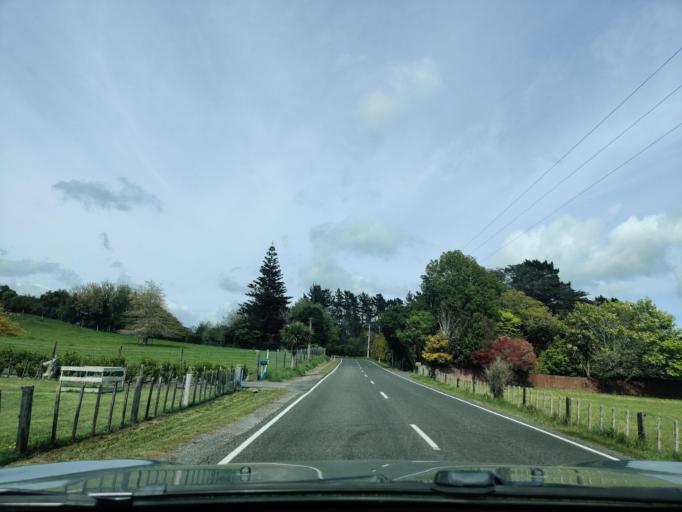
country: NZ
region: Taranaki
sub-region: New Plymouth District
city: New Plymouth
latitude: -39.1162
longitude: 174.0962
